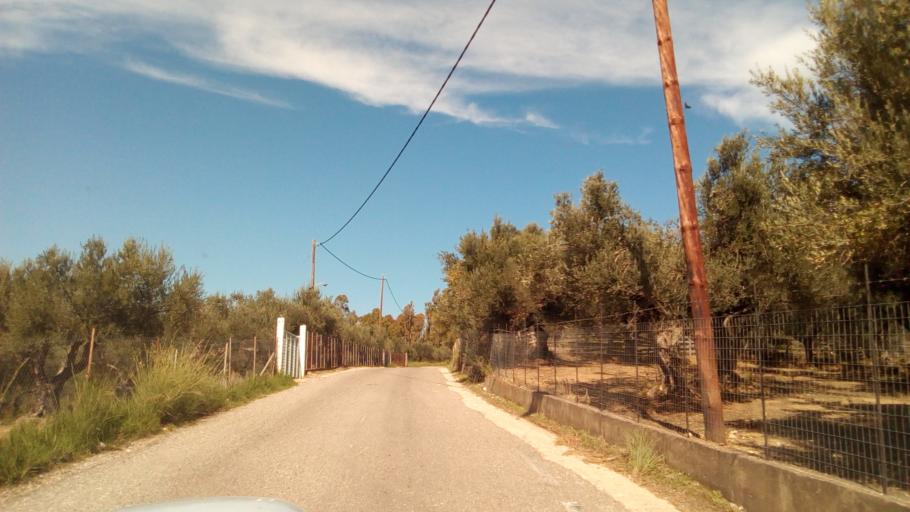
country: GR
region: West Greece
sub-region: Nomos Aitolias kai Akarnanias
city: Antirrio
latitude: 38.3412
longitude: 21.7554
